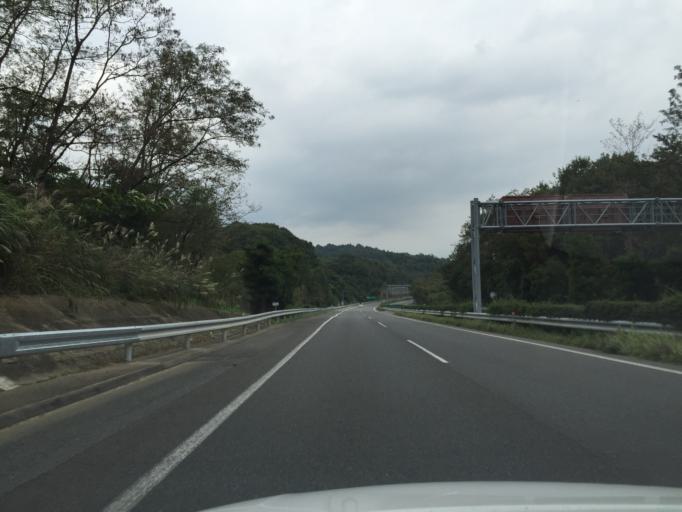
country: JP
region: Fukushima
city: Iwaki
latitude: 37.0455
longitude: 140.8208
